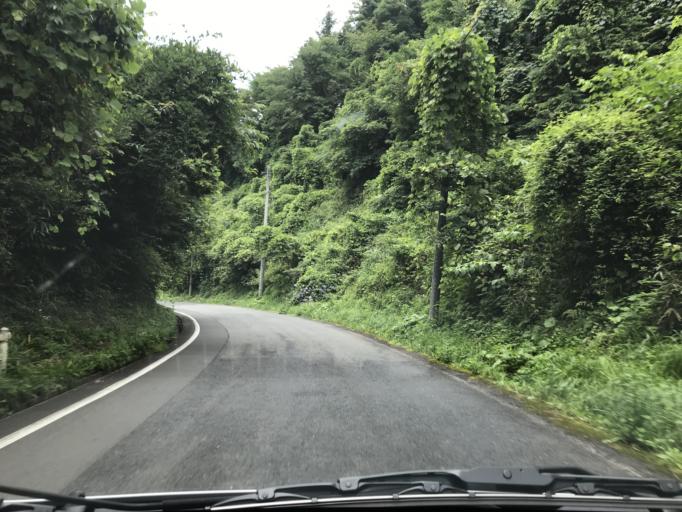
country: JP
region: Iwate
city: Mizusawa
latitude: 39.0339
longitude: 141.3505
